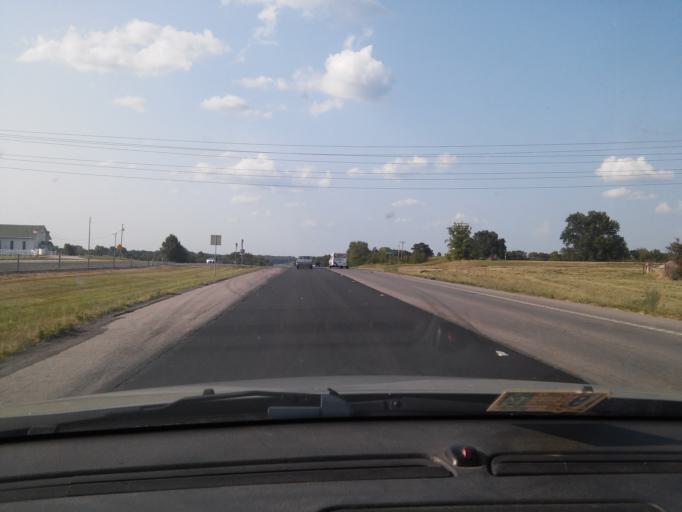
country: US
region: Missouri
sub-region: Boone County
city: Ashland
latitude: 38.7979
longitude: -92.2515
